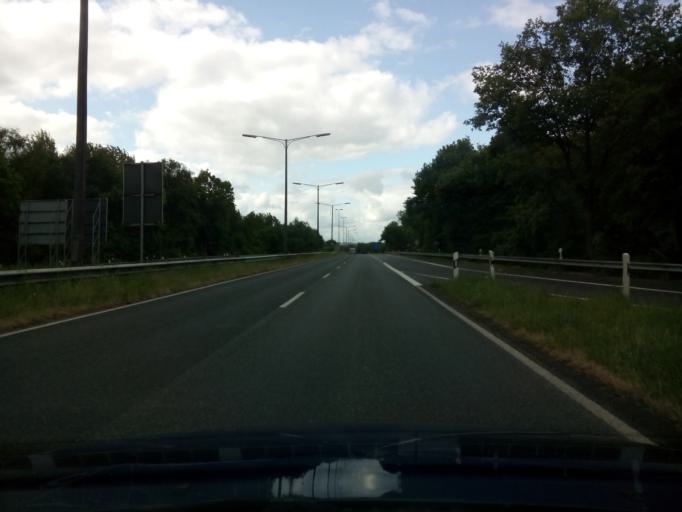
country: DE
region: Lower Saxony
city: Lilienthal
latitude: 53.1117
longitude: 8.8683
